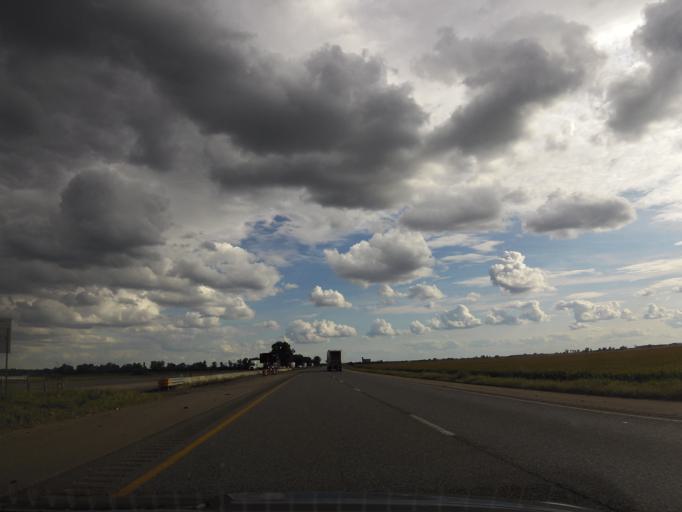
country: US
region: Indiana
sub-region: Porter County
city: Hebron
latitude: 41.2617
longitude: -87.2958
